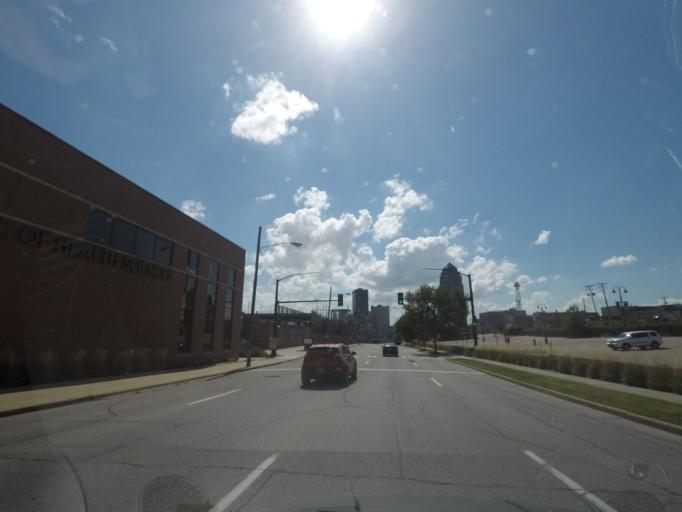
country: US
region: Iowa
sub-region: Polk County
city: Des Moines
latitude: 41.5947
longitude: -93.6269
